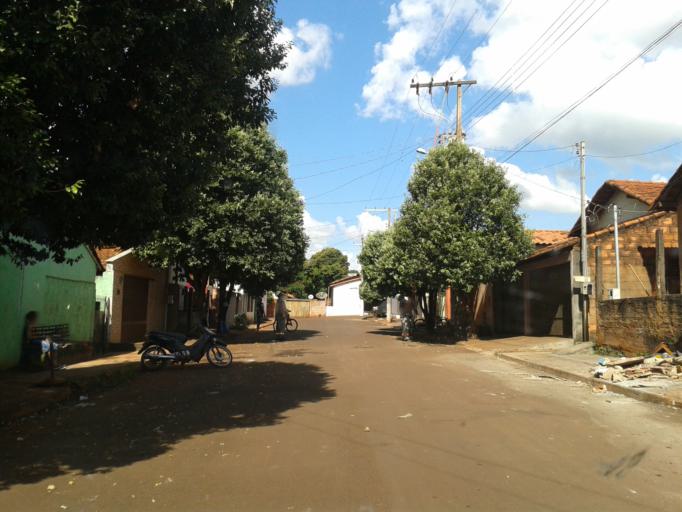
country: BR
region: Minas Gerais
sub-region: Capinopolis
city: Capinopolis
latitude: -18.6857
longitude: -49.5808
